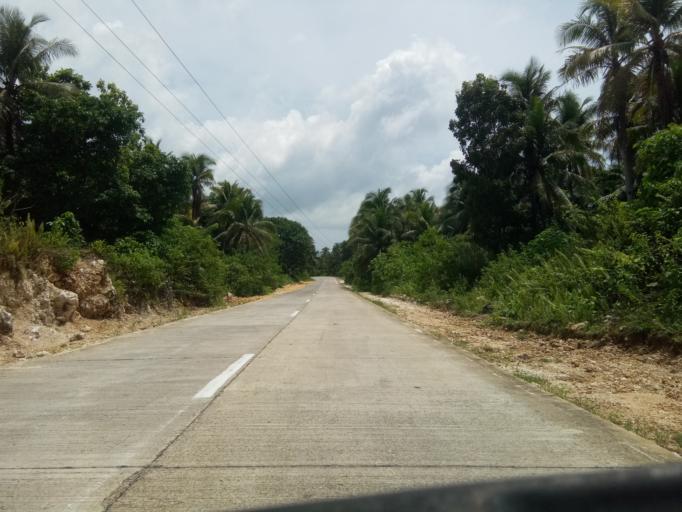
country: PH
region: Caraga
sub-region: Province of Surigao del Norte
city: San Isidro
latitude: 9.9289
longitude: 126.0990
